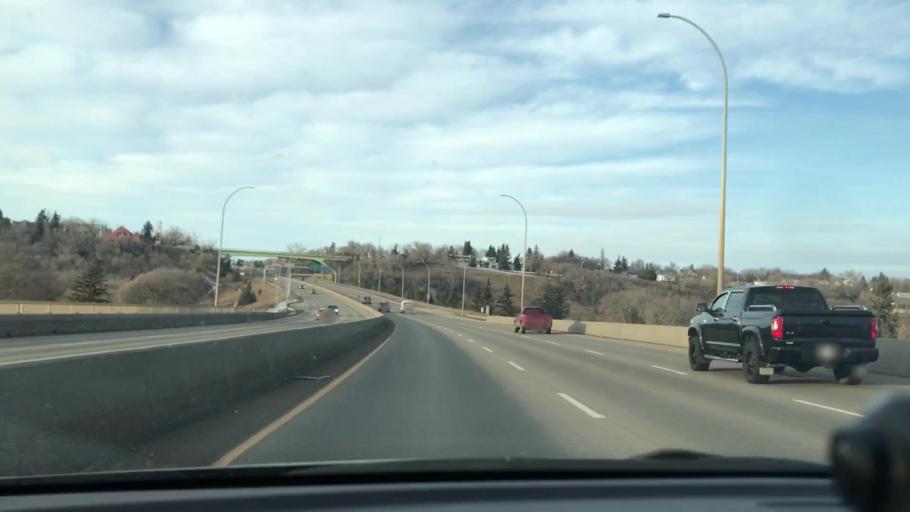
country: CA
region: Alberta
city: Edmonton
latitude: 53.5562
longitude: -113.4391
